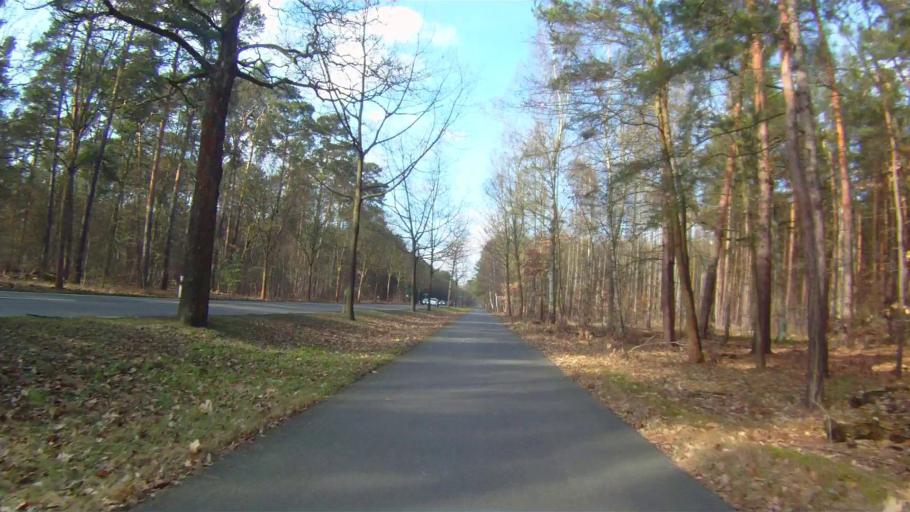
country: DE
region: Brandenburg
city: Zeuthen
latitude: 52.3911
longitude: 13.6226
